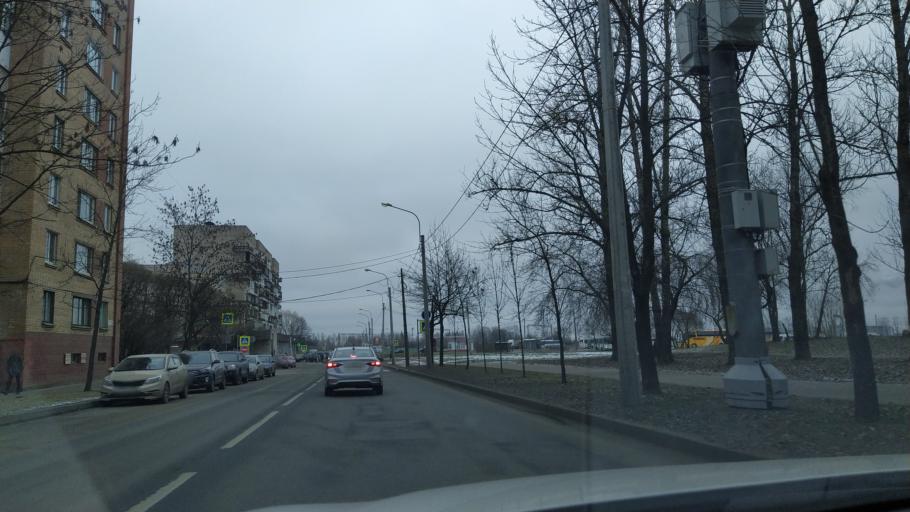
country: RU
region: St.-Petersburg
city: Pushkin
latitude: 59.7293
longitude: 30.4210
